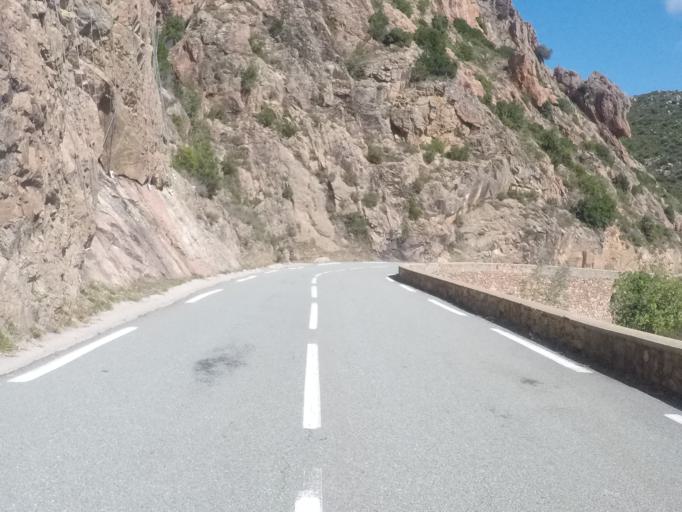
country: FR
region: Corsica
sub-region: Departement de la Corse-du-Sud
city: Zonza
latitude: 41.7688
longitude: 9.0434
